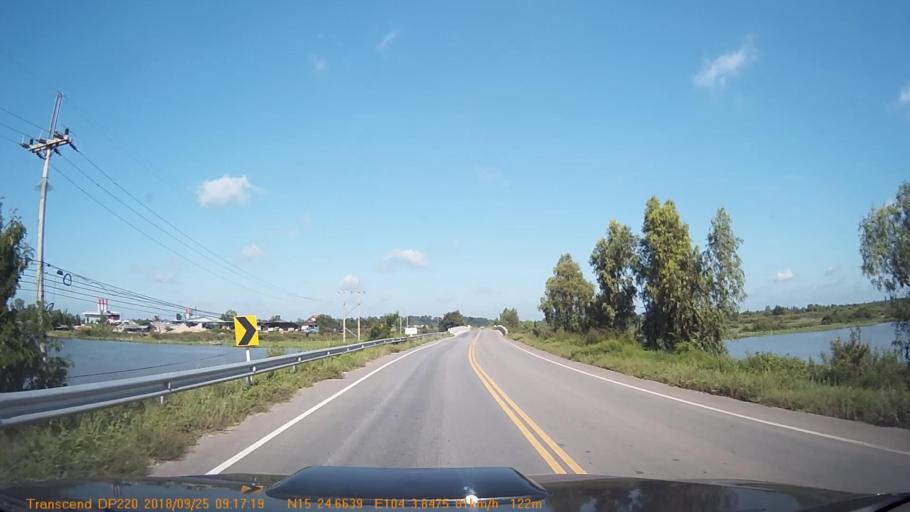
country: TH
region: Sisaket
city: Sila Lat
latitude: 15.4111
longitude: 104.0641
